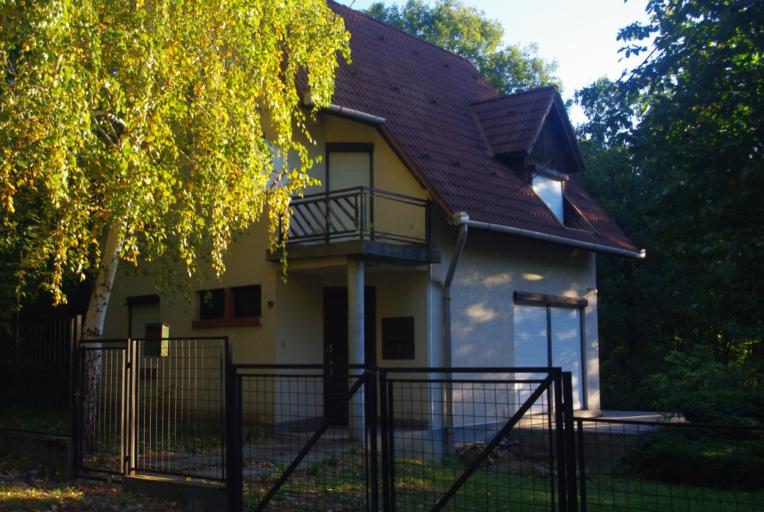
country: HU
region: Heves
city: Gyongyossolymos
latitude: 47.8344
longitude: 19.9622
